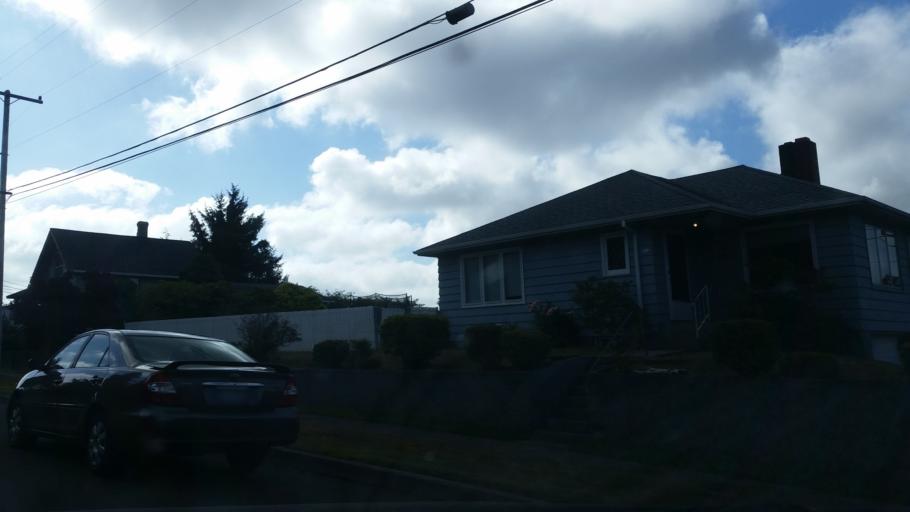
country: US
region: Oregon
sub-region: Clatsop County
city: Astoria
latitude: 46.1812
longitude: -123.8340
